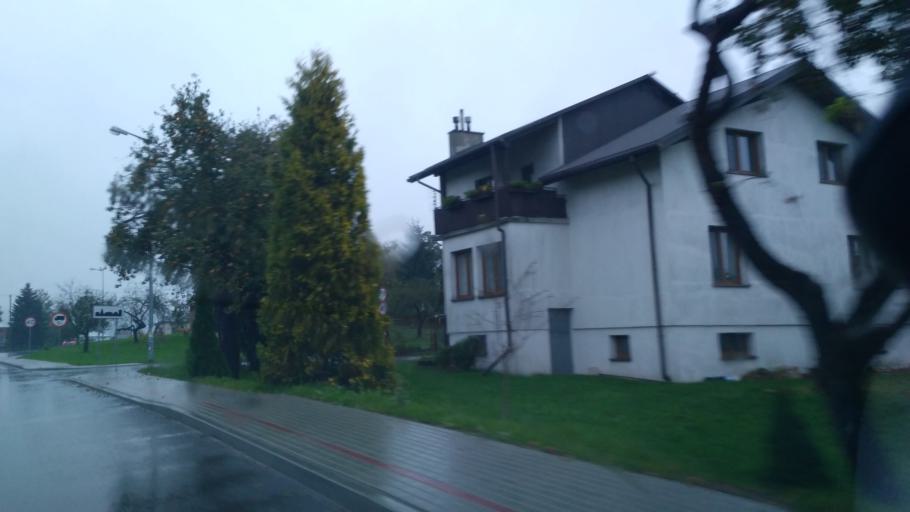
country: PL
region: Subcarpathian Voivodeship
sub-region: Powiat krosnienski
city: Korczyna
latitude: 49.6993
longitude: 21.8111
